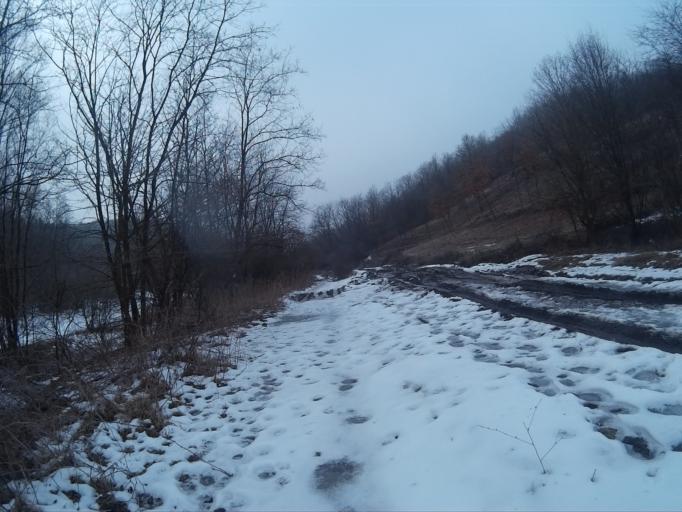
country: HU
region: Nograd
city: Tar
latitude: 47.9930
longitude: 19.7363
